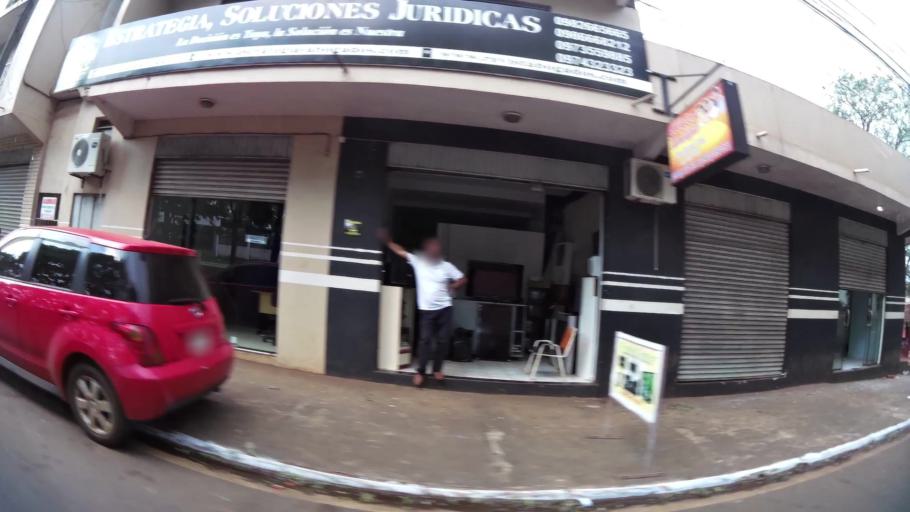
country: PY
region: Alto Parana
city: Ciudad del Este
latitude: -25.5201
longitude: -54.6111
